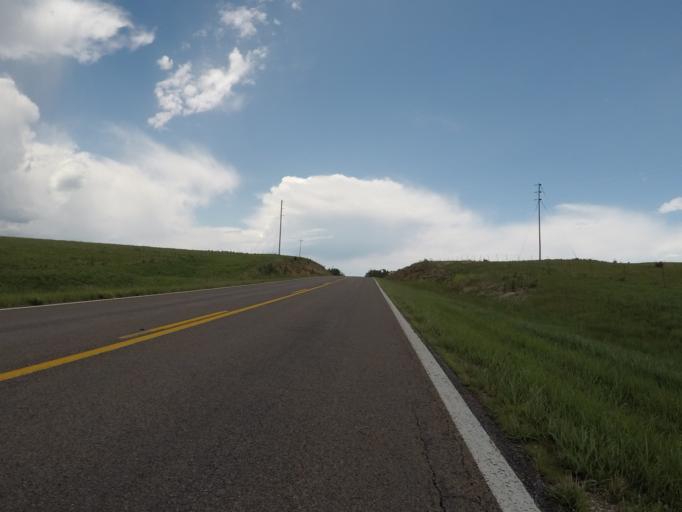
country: US
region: Kansas
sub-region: Wabaunsee County
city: Alma
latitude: 38.8691
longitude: -96.3296
